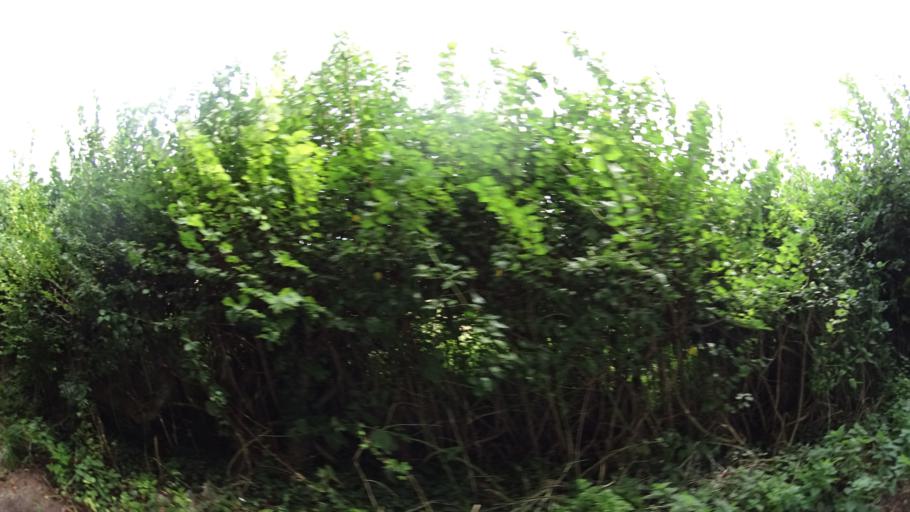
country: GB
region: England
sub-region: Dorset
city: Wimborne Minster
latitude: 50.8935
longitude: -2.0347
